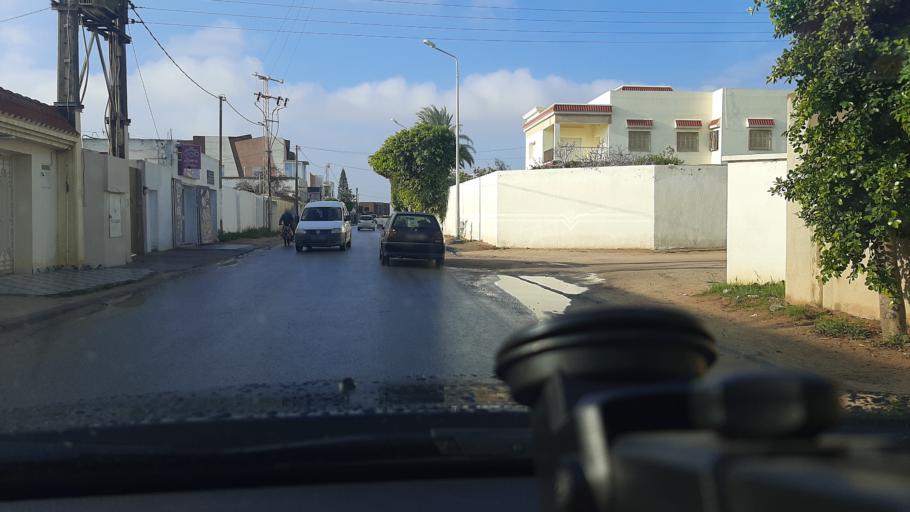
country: TN
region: Safaqis
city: Sfax
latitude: 34.7445
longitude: 10.7190
